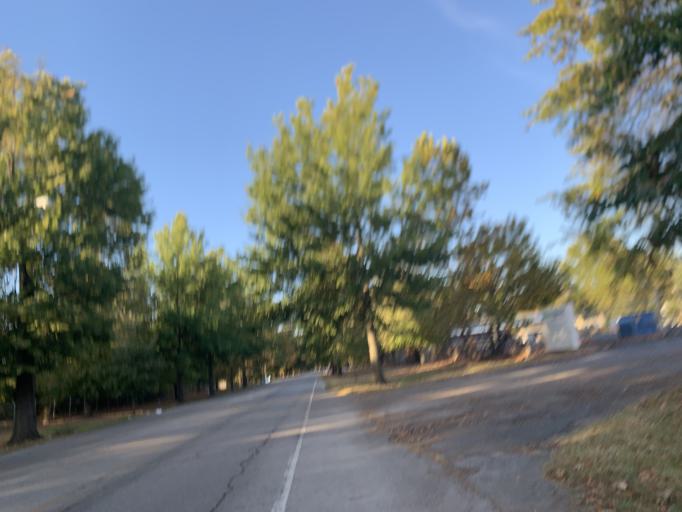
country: US
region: Kentucky
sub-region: Jefferson County
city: Shively
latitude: 38.2374
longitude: -85.8308
